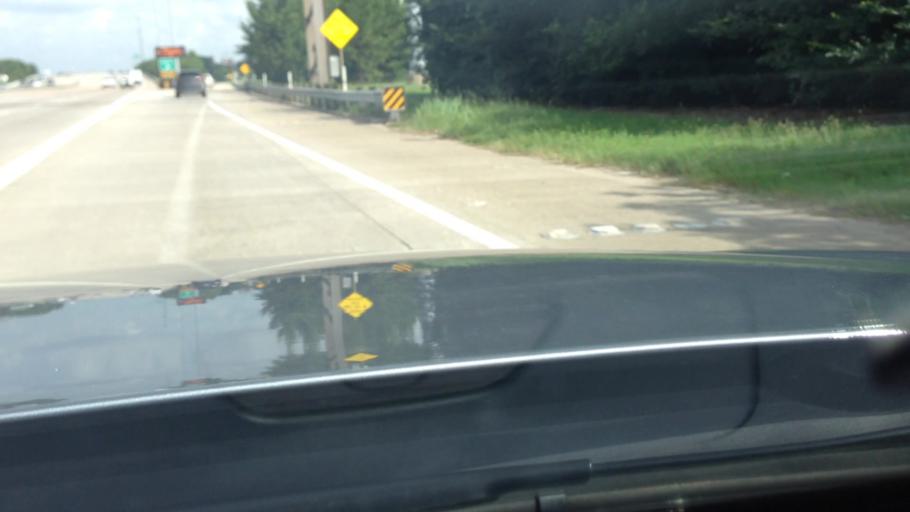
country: US
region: Texas
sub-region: Harris County
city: Hudson
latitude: 29.9498
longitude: -95.5326
